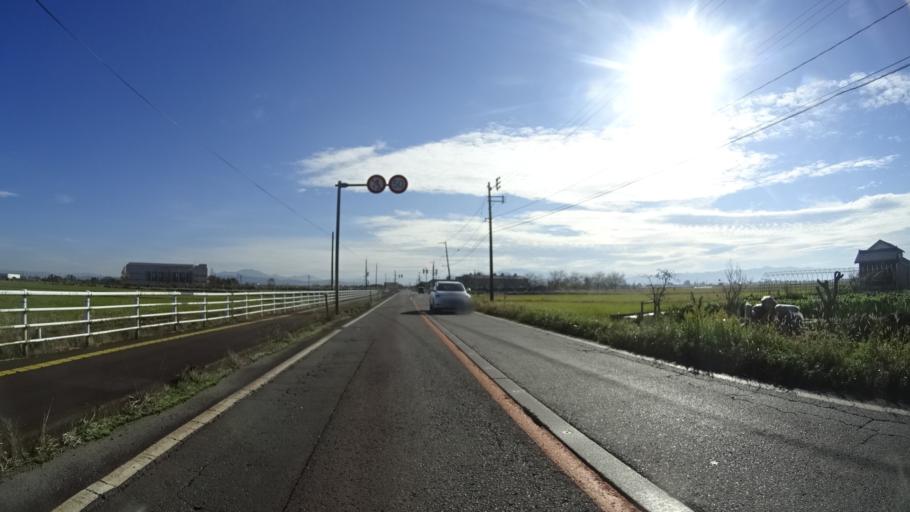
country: JP
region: Niigata
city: Mitsuke
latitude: 37.5539
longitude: 138.8585
